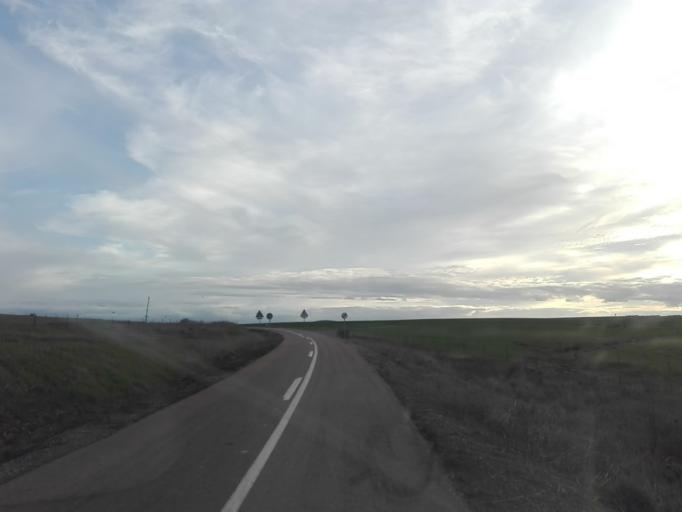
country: ES
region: Extremadura
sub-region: Provincia de Badajoz
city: Usagre
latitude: 38.4035
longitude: -6.1731
